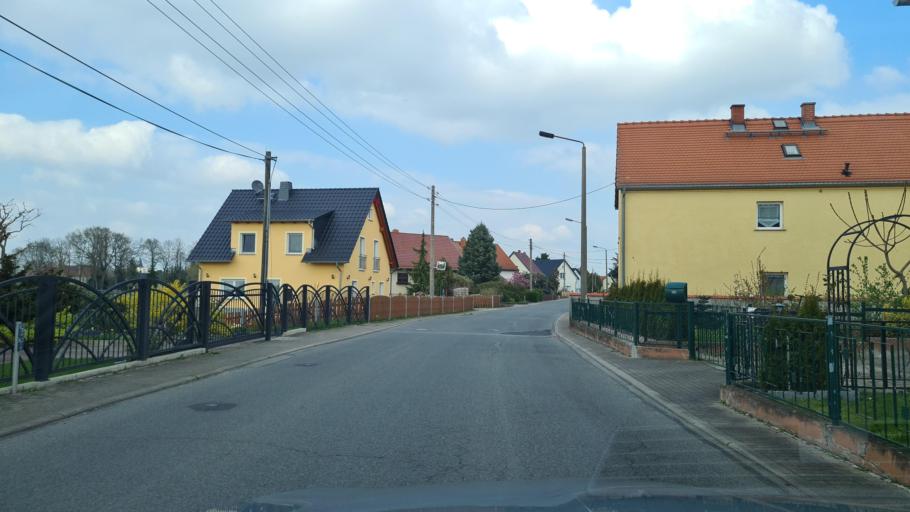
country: DE
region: Saxony
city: Wulknitz
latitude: 51.3756
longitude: 13.4245
